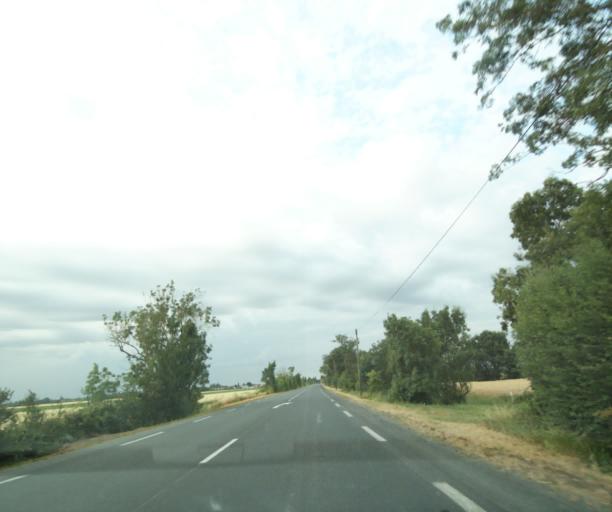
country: FR
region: Poitou-Charentes
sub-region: Departement de la Charente-Maritime
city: Marans
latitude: 46.3567
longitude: -0.9924
